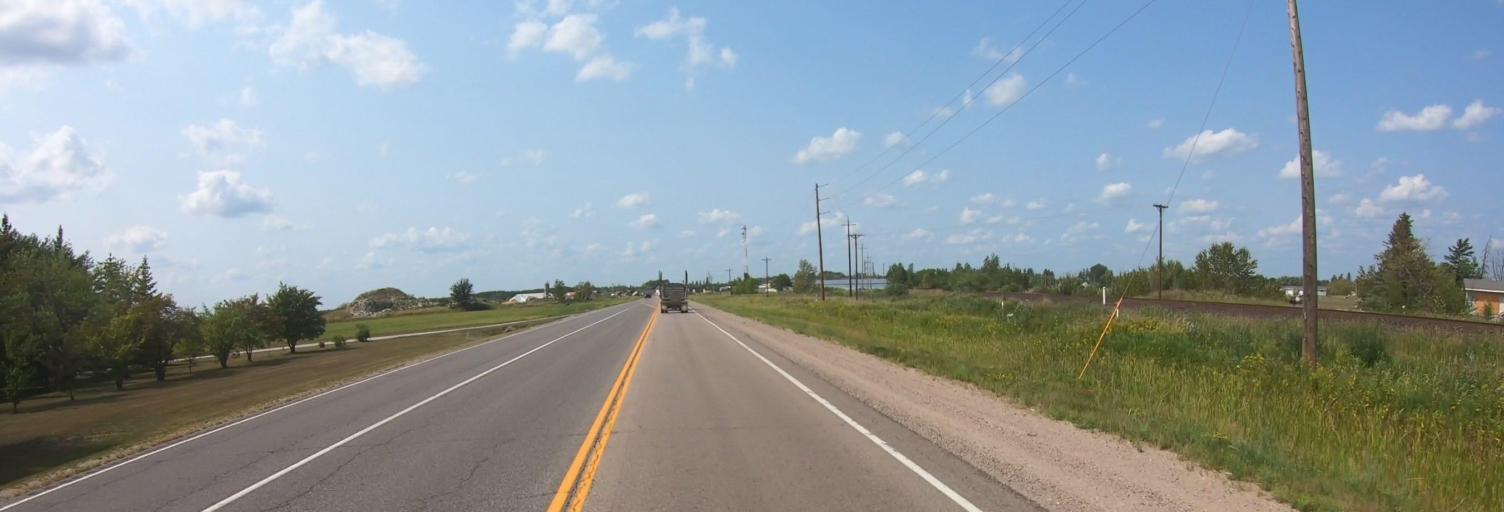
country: US
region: Minnesota
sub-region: Roseau County
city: Warroad
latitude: 48.8934
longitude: -95.3110
